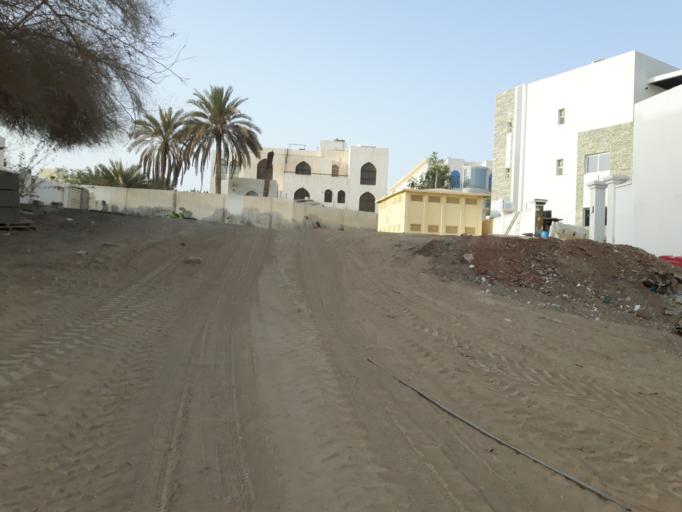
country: OM
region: Muhafazat Masqat
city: Bawshar
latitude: 23.6101
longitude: 58.4728
